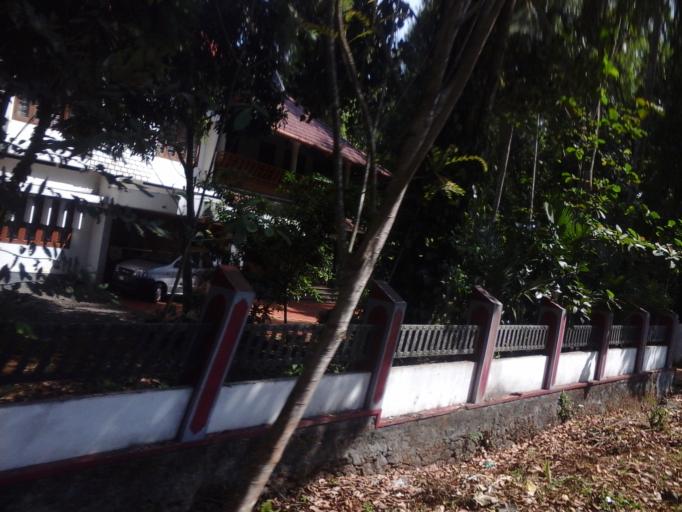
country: IN
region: Kerala
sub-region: Kottayam
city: Erattupetta
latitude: 9.7021
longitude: 76.7560
